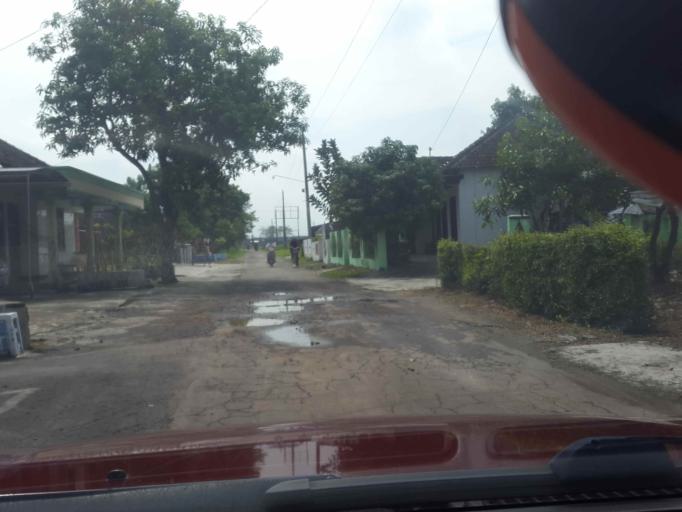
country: ID
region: Central Java
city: Jaten
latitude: -7.6018
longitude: 110.9245
